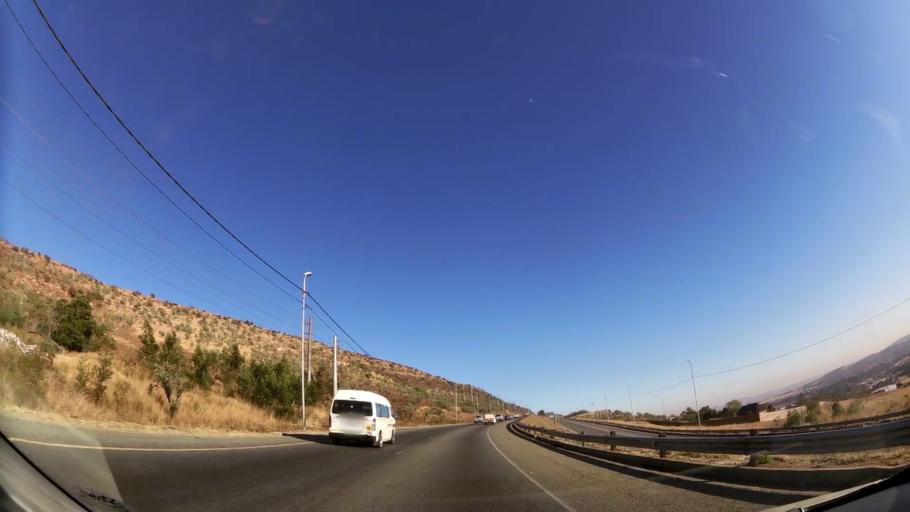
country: ZA
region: Gauteng
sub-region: West Rand District Municipality
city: Muldersdriseloop
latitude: -26.0677
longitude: 27.8202
